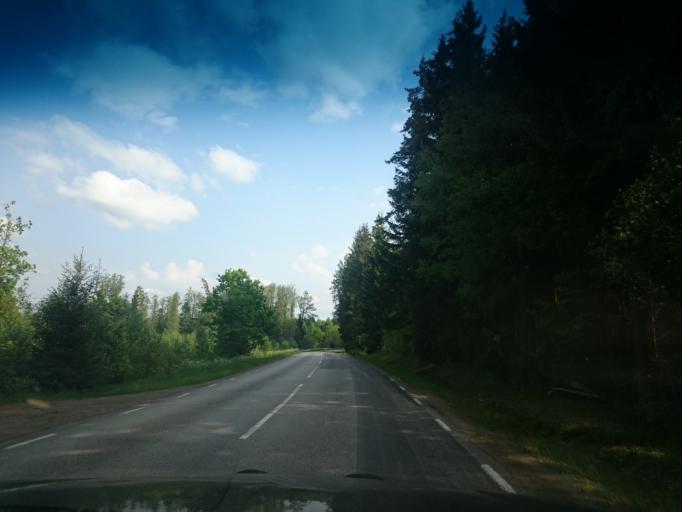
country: SE
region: Joenkoeping
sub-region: Vetlanda Kommun
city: Vetlanda
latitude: 57.3689
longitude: 15.0547
